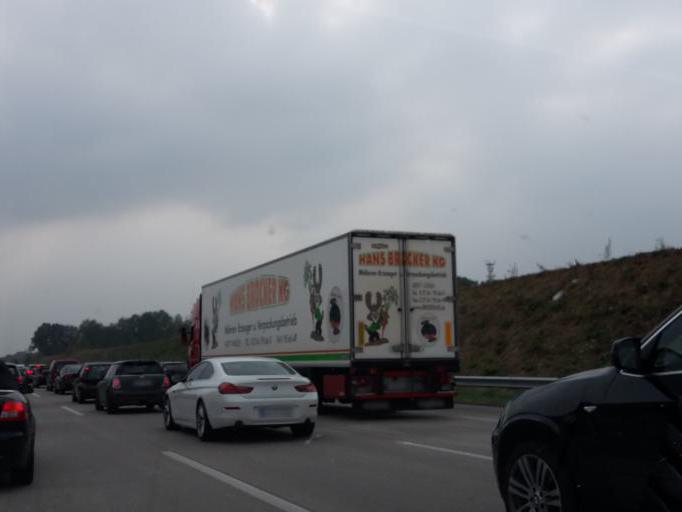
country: DE
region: Lower Saxony
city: Bakum
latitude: 52.7522
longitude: 8.1811
